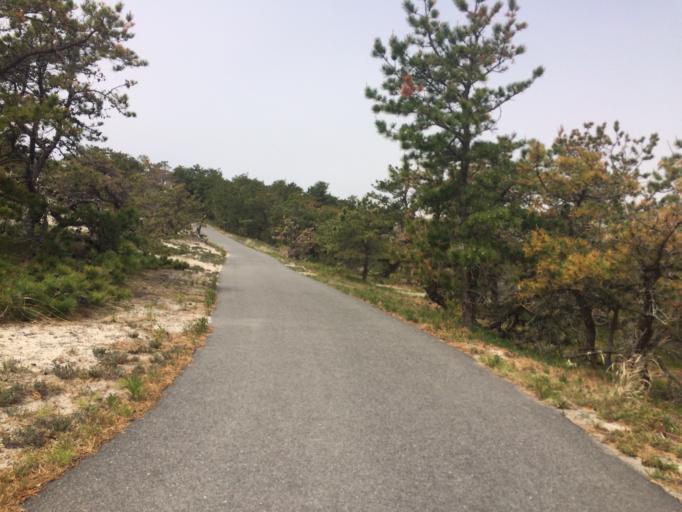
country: US
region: Massachusetts
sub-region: Barnstable County
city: Provincetown
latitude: 42.0752
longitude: -70.2032
